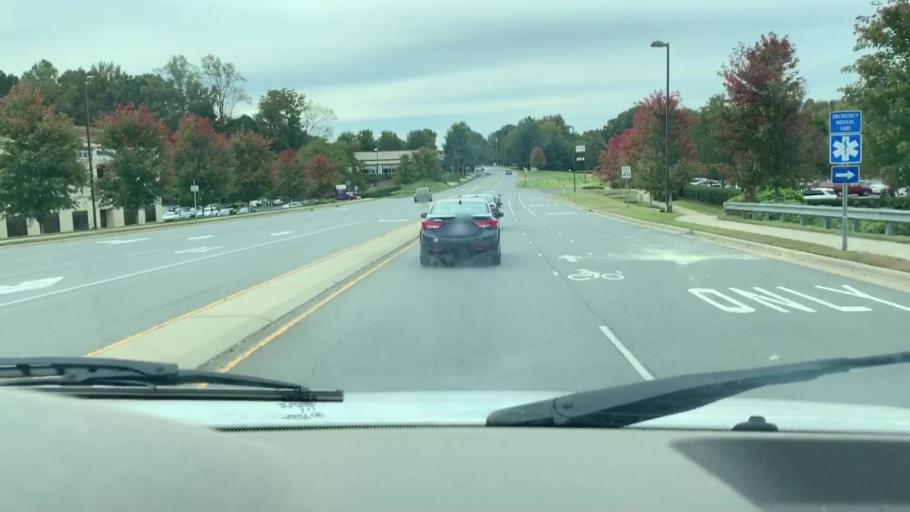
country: US
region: North Carolina
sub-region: Mecklenburg County
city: Huntersville
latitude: 35.4400
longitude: -80.8654
